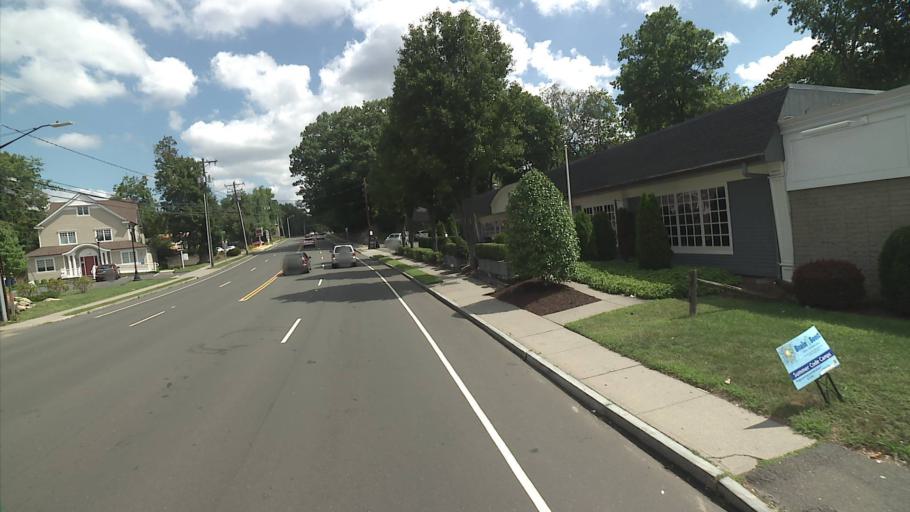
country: US
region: Connecticut
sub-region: Fairfield County
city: Riverside
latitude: 41.0445
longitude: -73.5724
